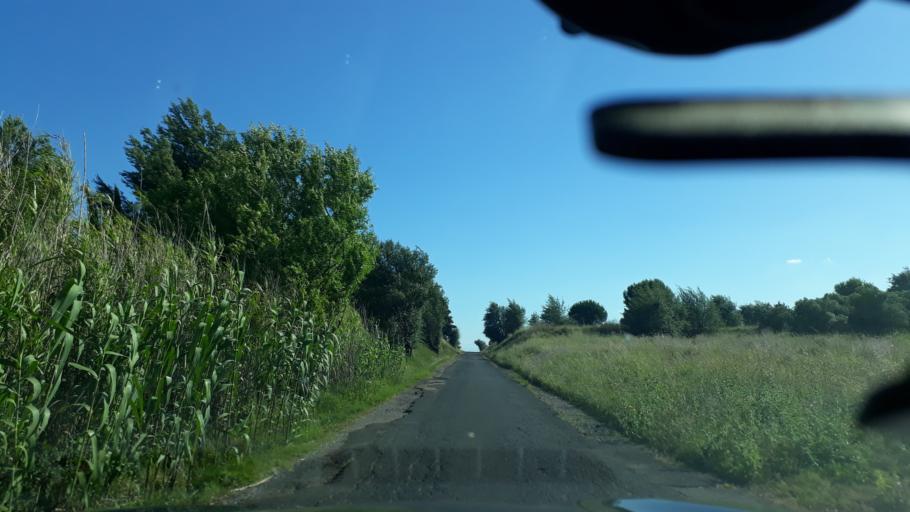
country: FR
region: Languedoc-Roussillon
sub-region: Departement de l'Herault
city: Marseillan
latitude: 43.3494
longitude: 3.5170
